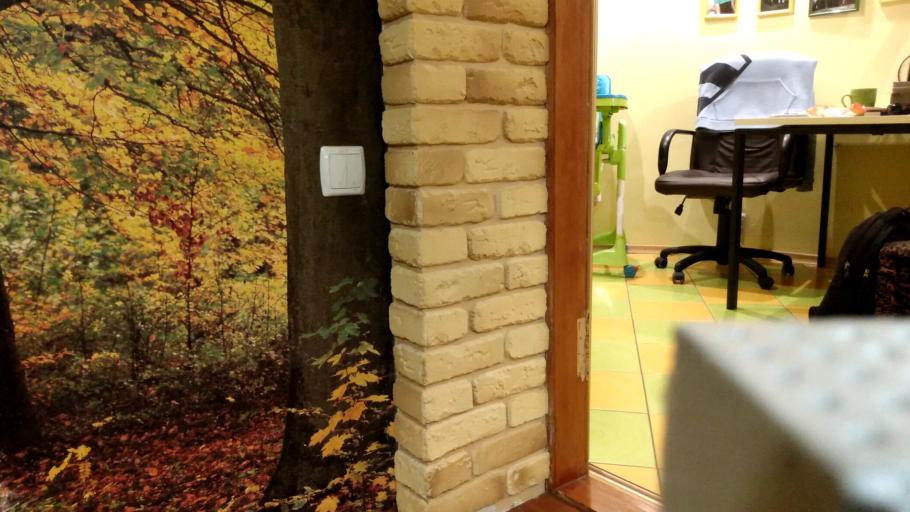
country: RU
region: Republic of Karelia
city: Pudozh
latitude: 61.7964
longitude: 37.6731
